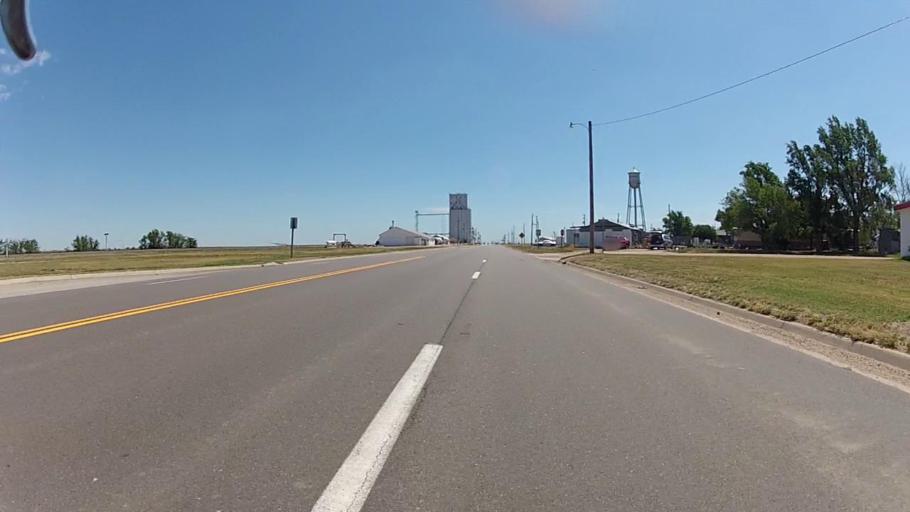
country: US
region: Kansas
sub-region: Gray County
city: Cimarron
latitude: 37.6539
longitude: -100.2326
